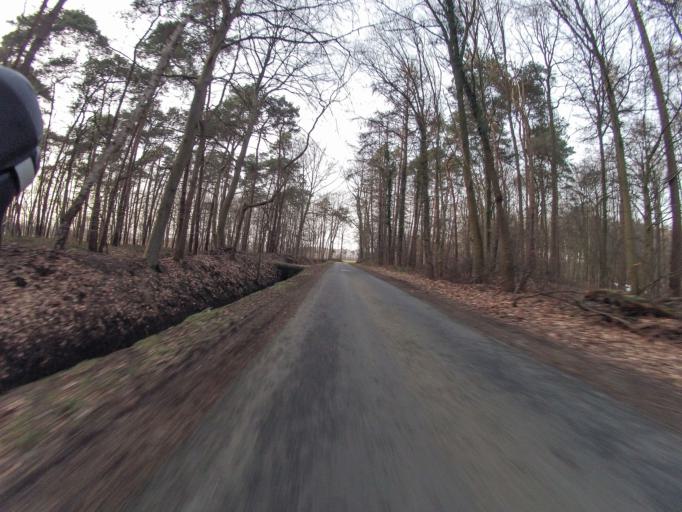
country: DE
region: North Rhine-Westphalia
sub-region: Regierungsbezirk Munster
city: Steinfurt
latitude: 52.1766
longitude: 7.3321
